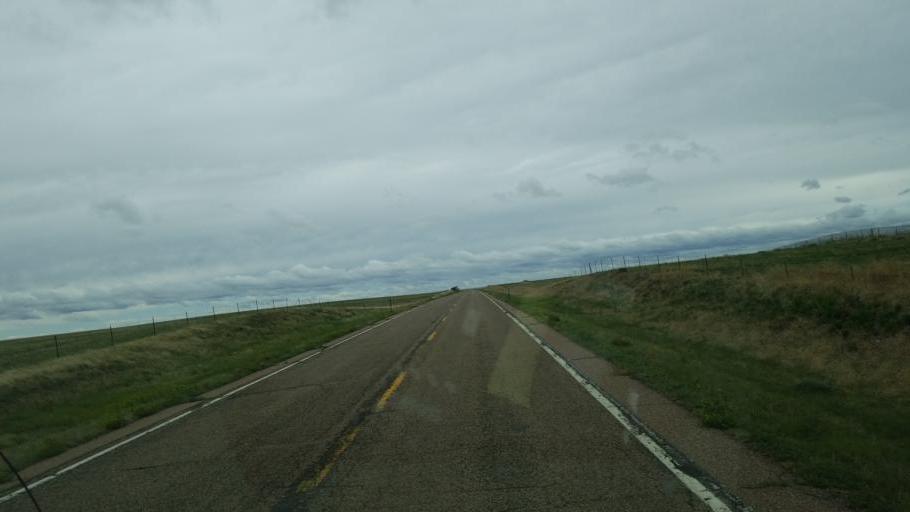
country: US
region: Colorado
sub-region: Lincoln County
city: Hugo
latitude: 38.8522
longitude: -103.7142
